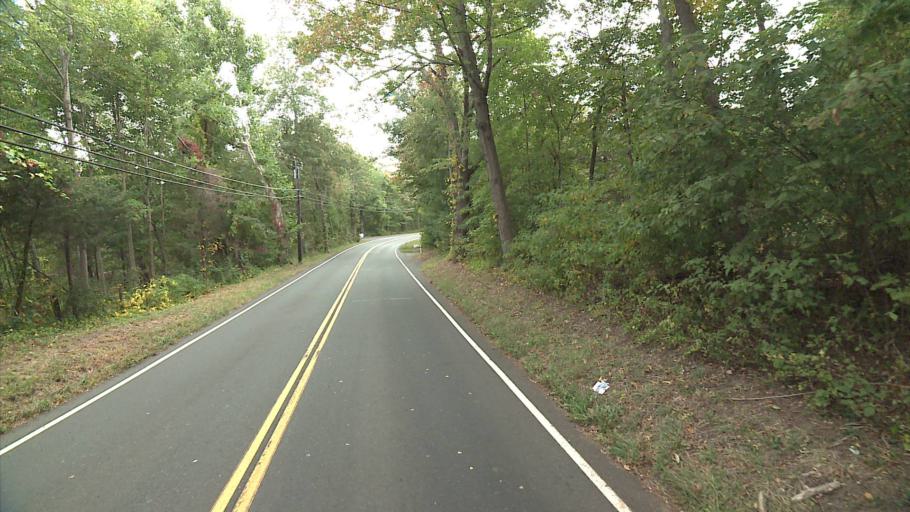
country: US
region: Connecticut
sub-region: Middlesex County
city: Durham
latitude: 41.4792
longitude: -72.7258
